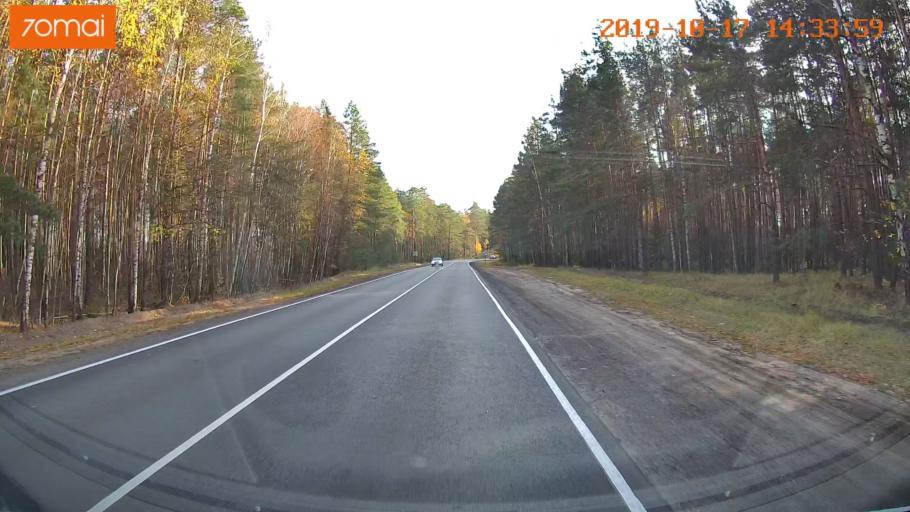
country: RU
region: Rjazan
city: Solotcha
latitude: 54.9178
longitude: 39.9968
